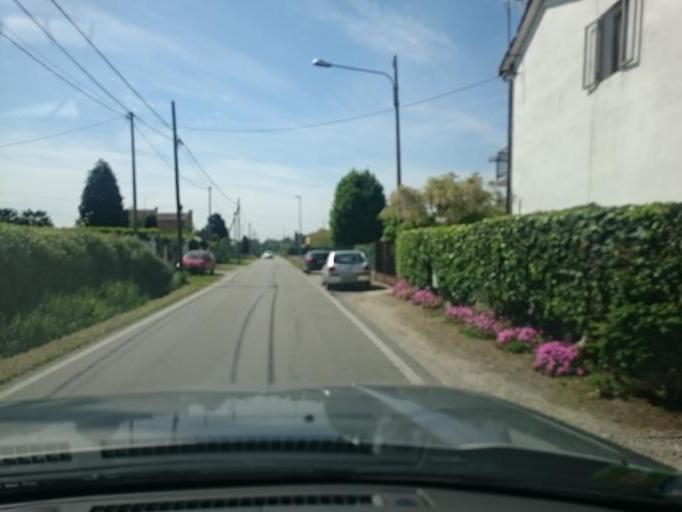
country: IT
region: Veneto
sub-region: Provincia di Padova
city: Bertipaglia
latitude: 45.3039
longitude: 11.8757
